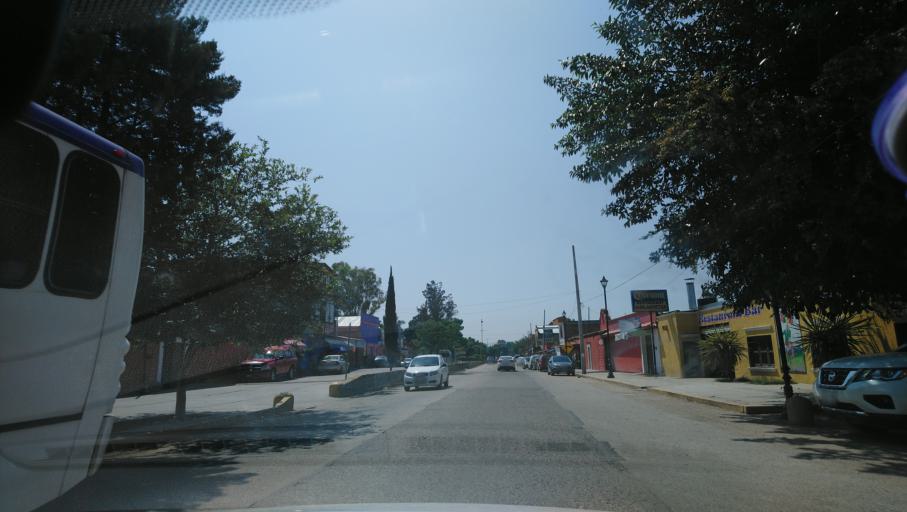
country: MX
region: Oaxaca
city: Santa Maria del Tule
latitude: 17.0460
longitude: -96.6383
